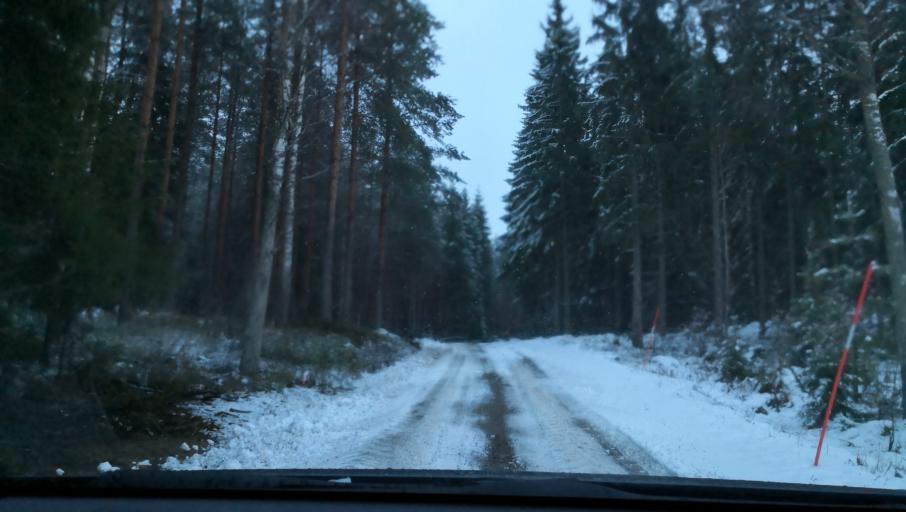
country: SE
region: Vaestmanland
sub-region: Kopings Kommun
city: Kolsva
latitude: 59.5596
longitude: 15.8427
